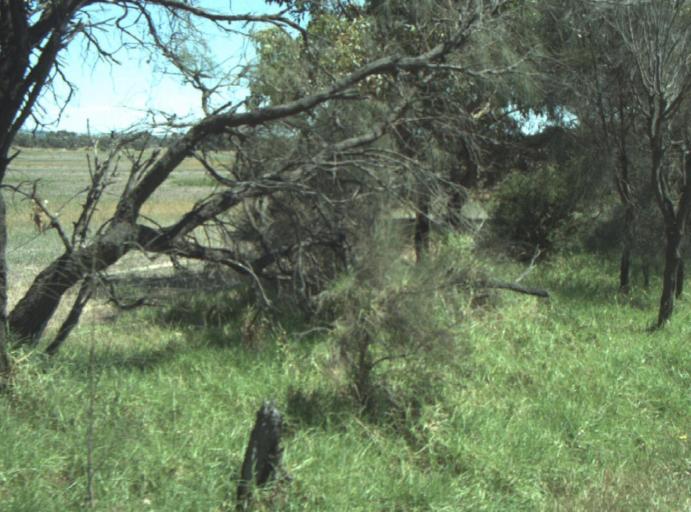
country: AU
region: Victoria
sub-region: Greater Geelong
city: Breakwater
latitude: -38.2130
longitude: 144.3581
